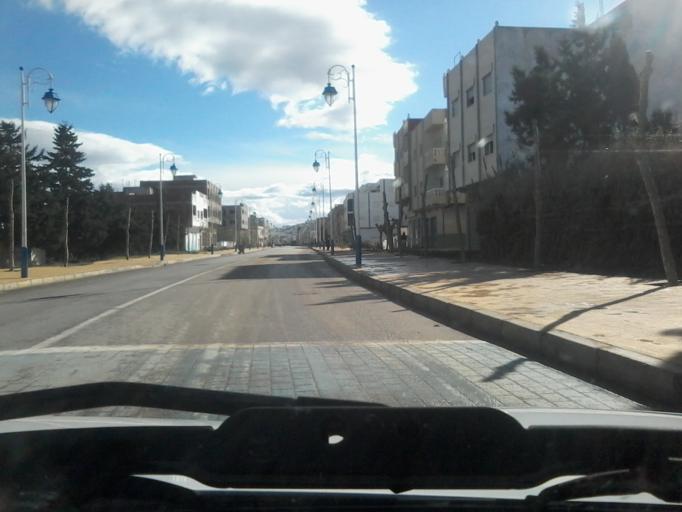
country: MA
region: Tanger-Tetouan
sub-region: Tetouan
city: Martil
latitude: 35.7019
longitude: -5.3507
